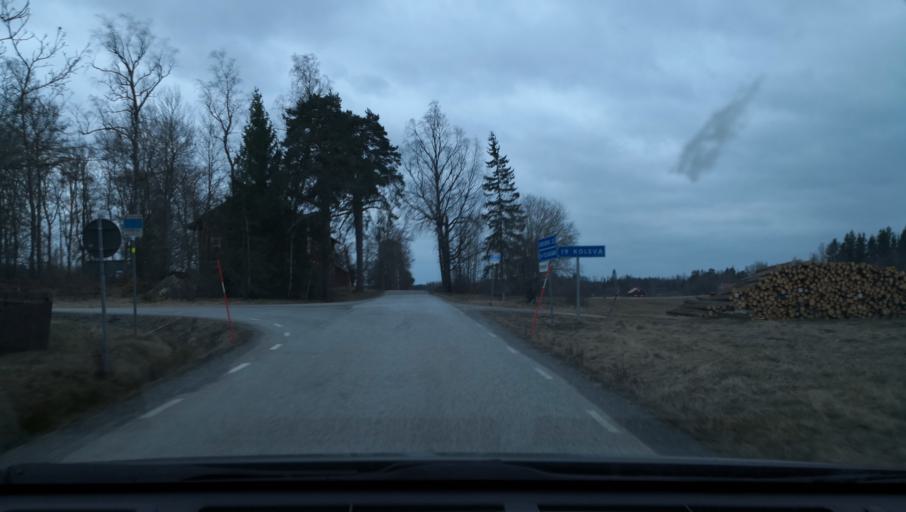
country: SE
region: OErebro
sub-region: Lindesbergs Kommun
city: Fellingsbro
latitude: 59.5621
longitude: 15.5787
